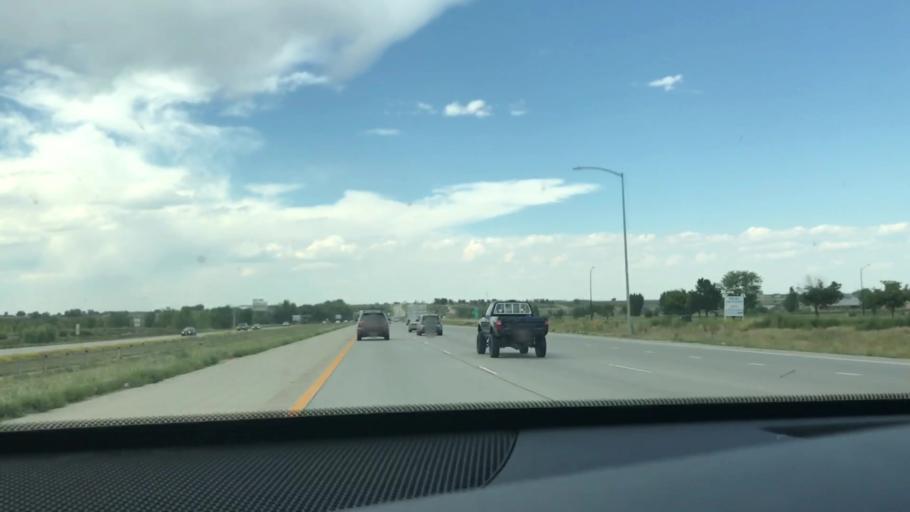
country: US
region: Colorado
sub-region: Weld County
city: Firestone
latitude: 40.1645
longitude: -104.9787
